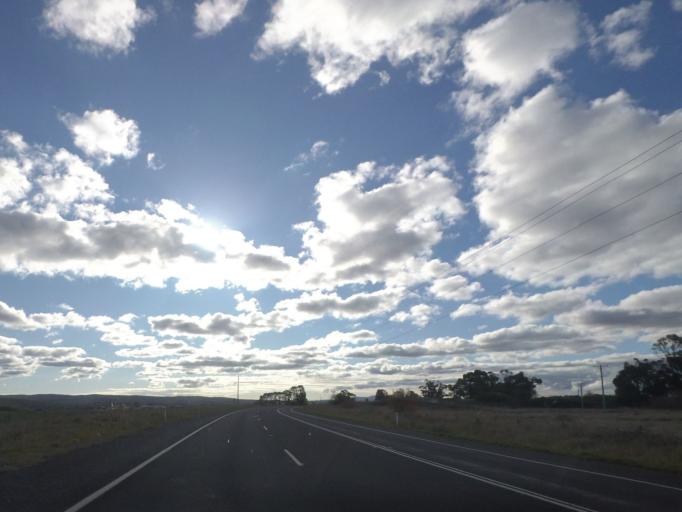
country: AU
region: Victoria
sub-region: Mount Alexander
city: Castlemaine
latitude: -37.1785
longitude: 144.3601
